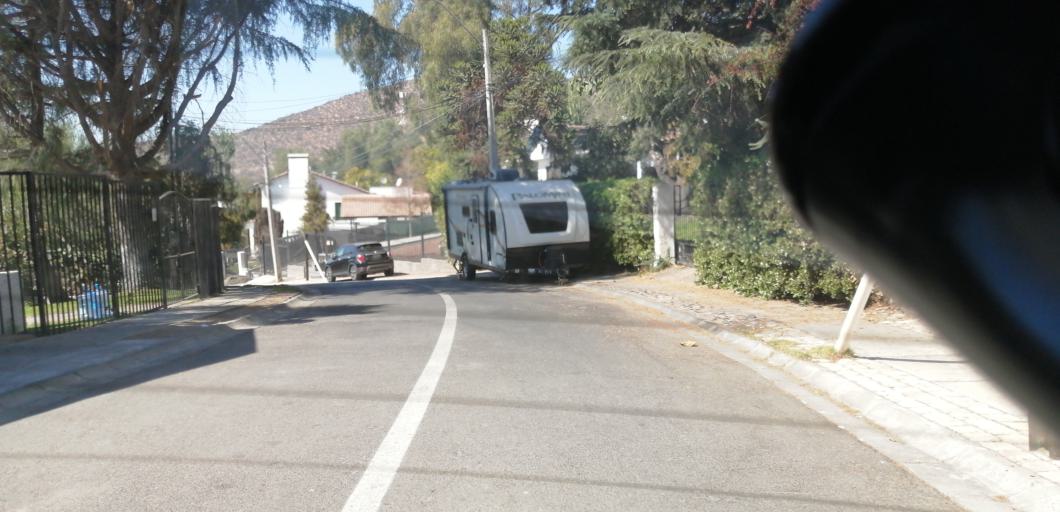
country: CL
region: Santiago Metropolitan
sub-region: Provincia de Santiago
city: Lo Prado
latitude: -33.4586
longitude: -70.8211
